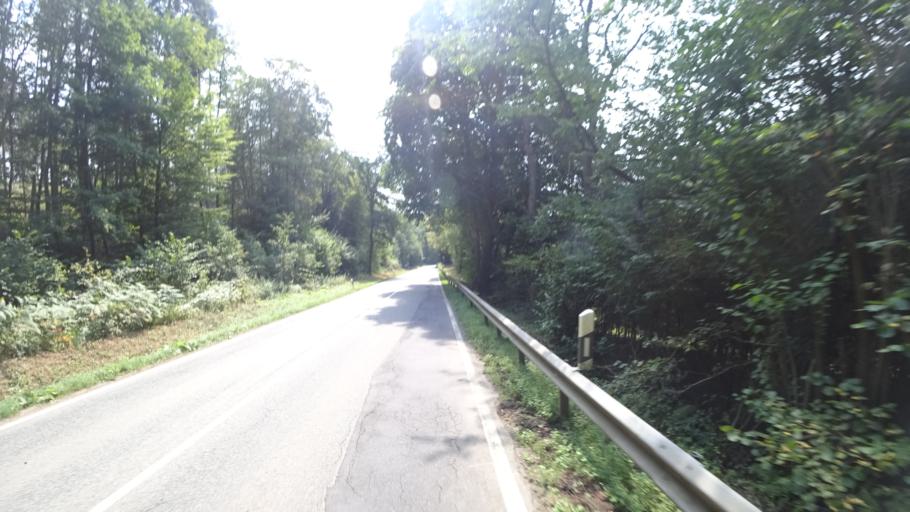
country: DE
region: Rheinland-Pfalz
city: Hohr-Grenzhausen
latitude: 50.4268
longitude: 7.6494
